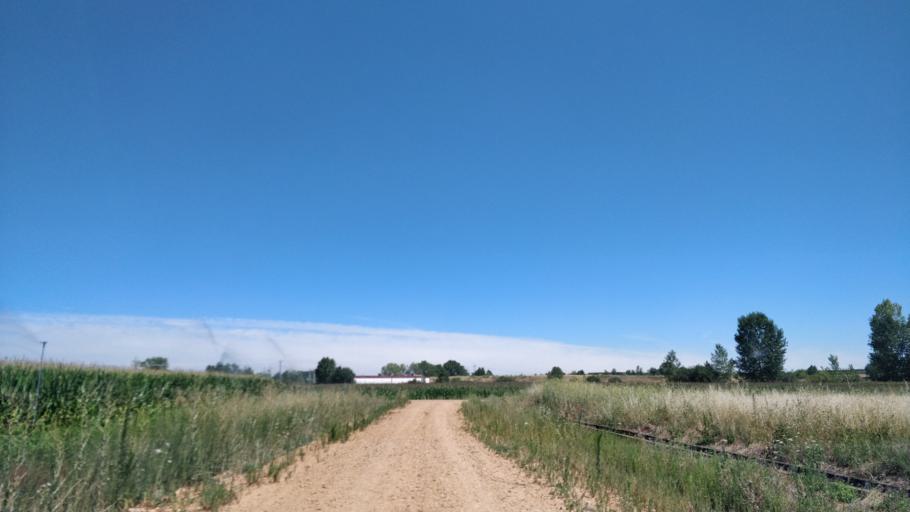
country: ES
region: Castille and Leon
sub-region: Provincia de Leon
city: Bustillo del Paramo
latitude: 42.4752
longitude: -5.8113
